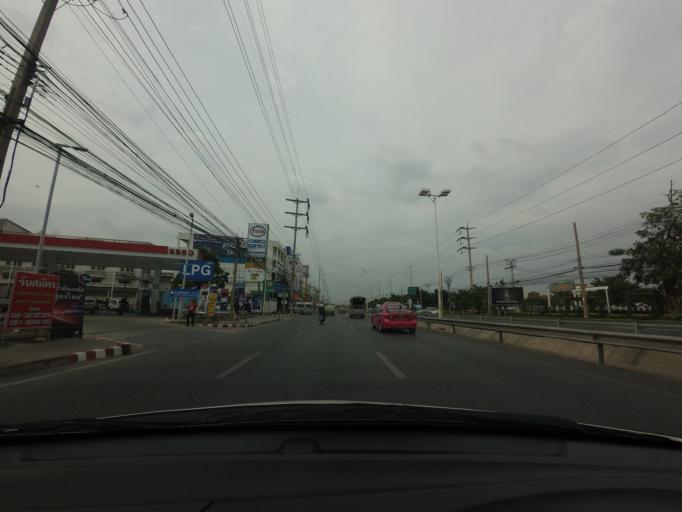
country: TH
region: Samut Prakan
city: Samut Prakan
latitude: 13.5450
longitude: 100.6185
